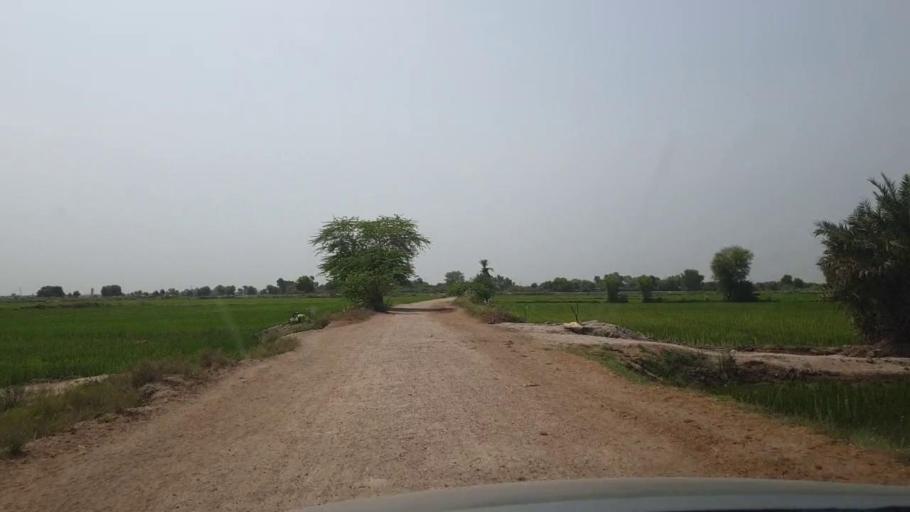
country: PK
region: Sindh
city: Madeji
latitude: 27.8012
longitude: 68.5390
